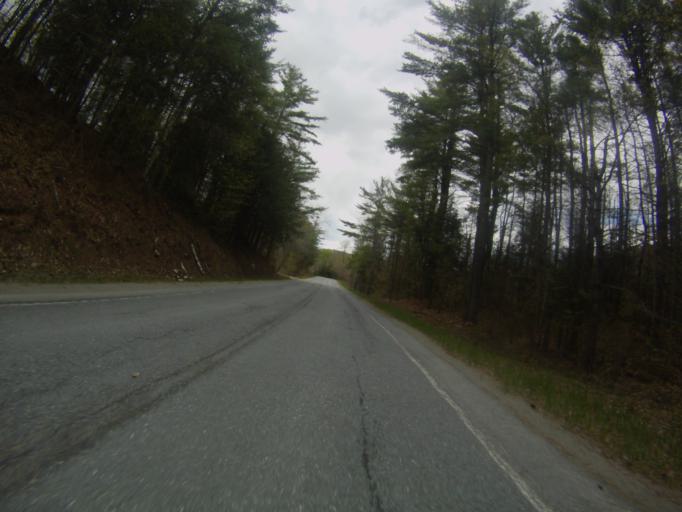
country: US
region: New York
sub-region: Essex County
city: Mineville
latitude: 44.0926
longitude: -73.5502
